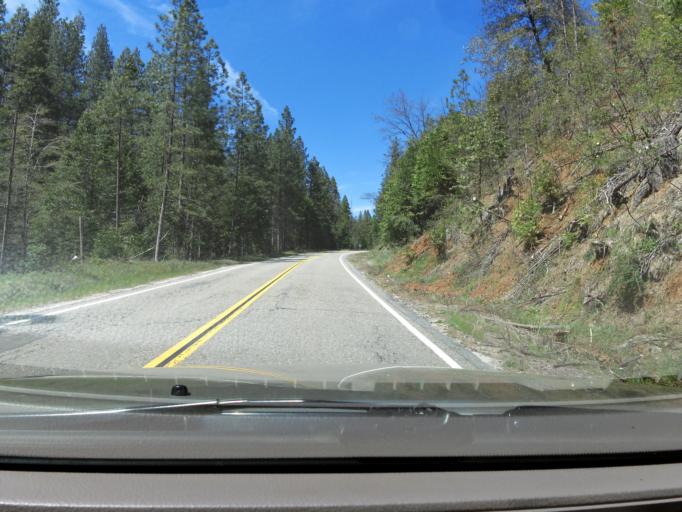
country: US
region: California
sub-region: Madera County
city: Oakhurst
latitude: 37.2820
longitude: -119.5764
